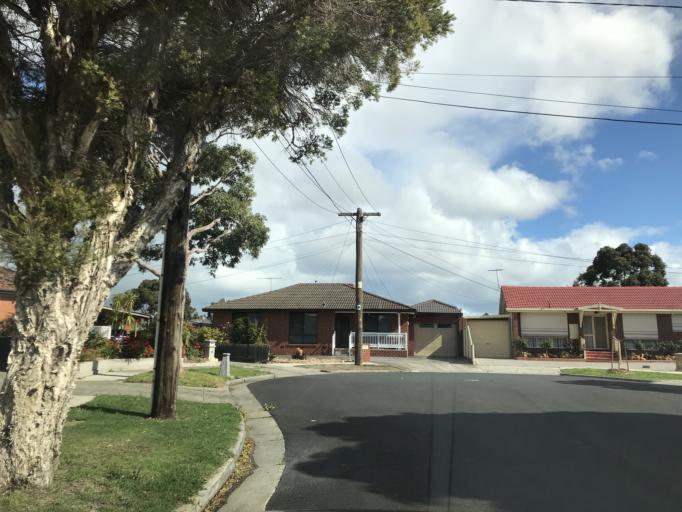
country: AU
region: Victoria
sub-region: Brimbank
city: Sunshine West
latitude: -37.7923
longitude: 144.7962
